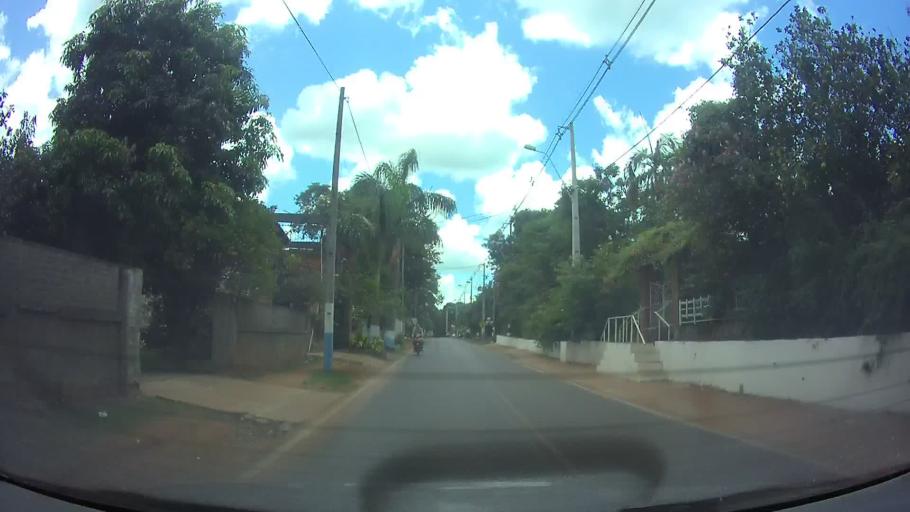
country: PY
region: Central
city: Aregua
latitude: -25.2965
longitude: -57.4411
